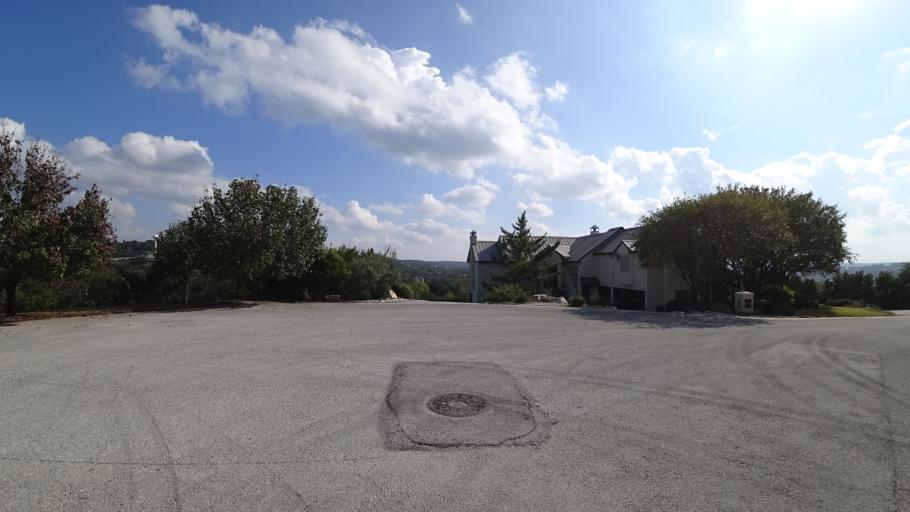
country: US
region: Texas
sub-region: Travis County
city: Lost Creek
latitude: 30.3093
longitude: -97.8515
